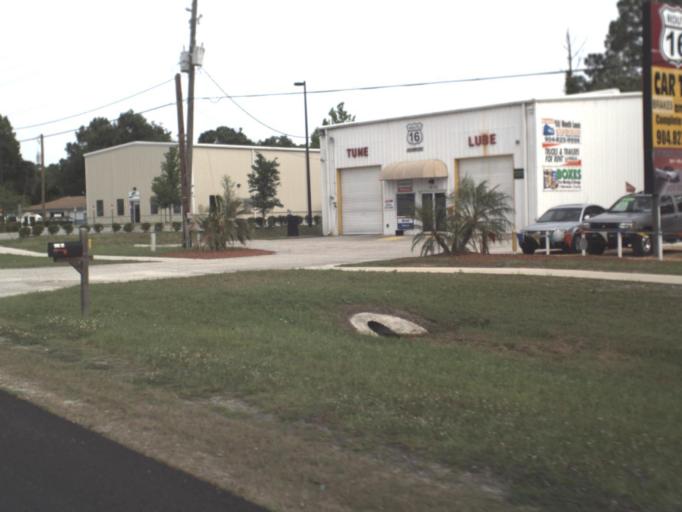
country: US
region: Florida
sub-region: Saint Johns County
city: Saint Augustine
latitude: 29.9139
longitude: -81.3941
